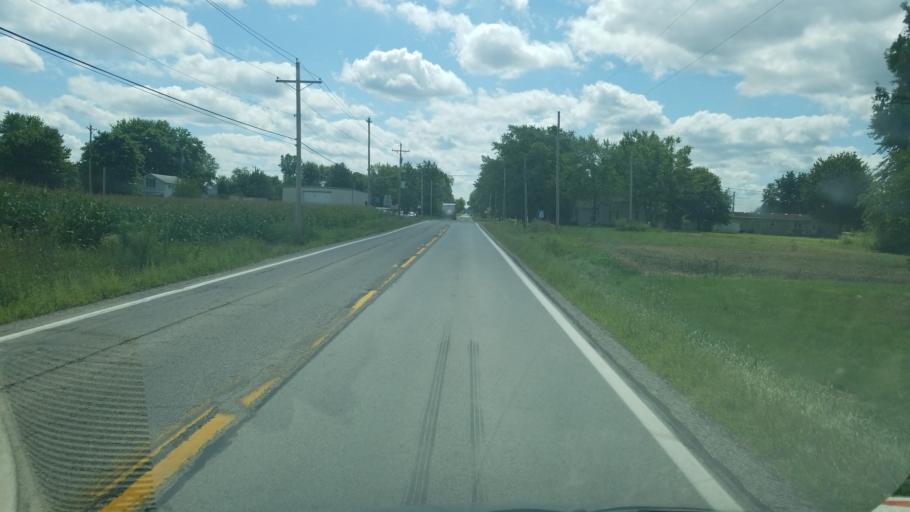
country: US
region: Ohio
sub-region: Henry County
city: Liberty Center
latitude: 41.4731
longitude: -84.0088
